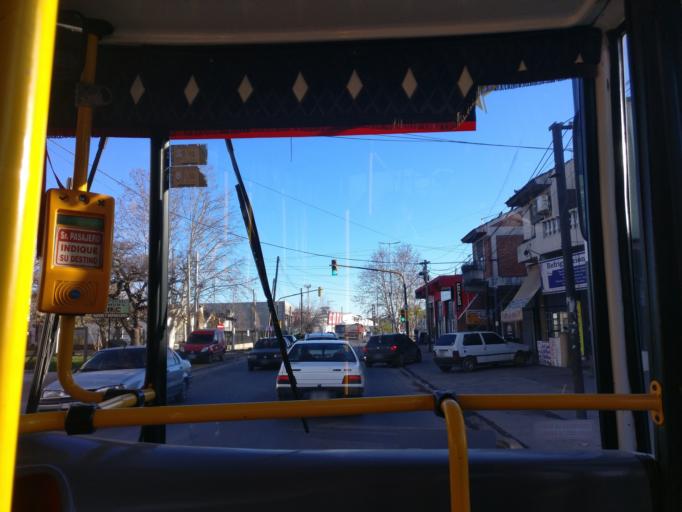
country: AR
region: Buenos Aires
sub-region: Partido de Ezeiza
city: Ezeiza
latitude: -34.8921
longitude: -58.5706
